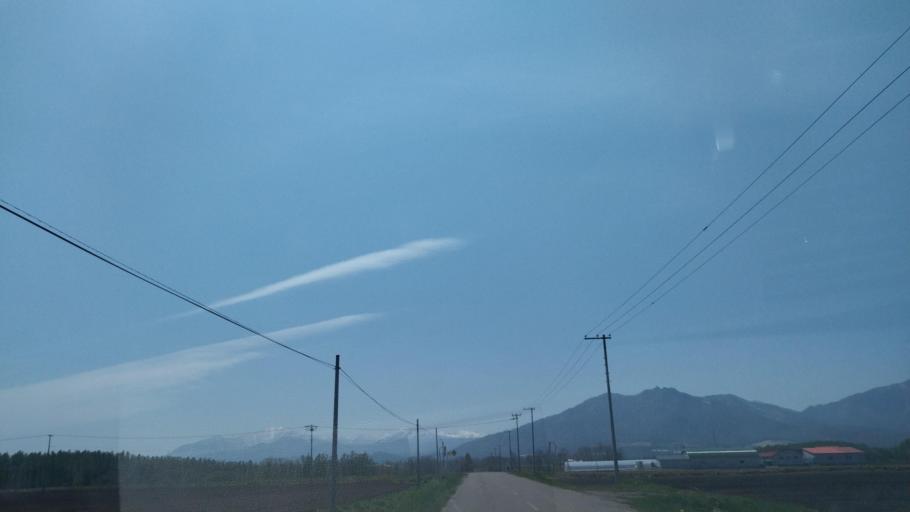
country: JP
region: Hokkaido
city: Obihiro
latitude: 42.9022
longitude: 142.9844
